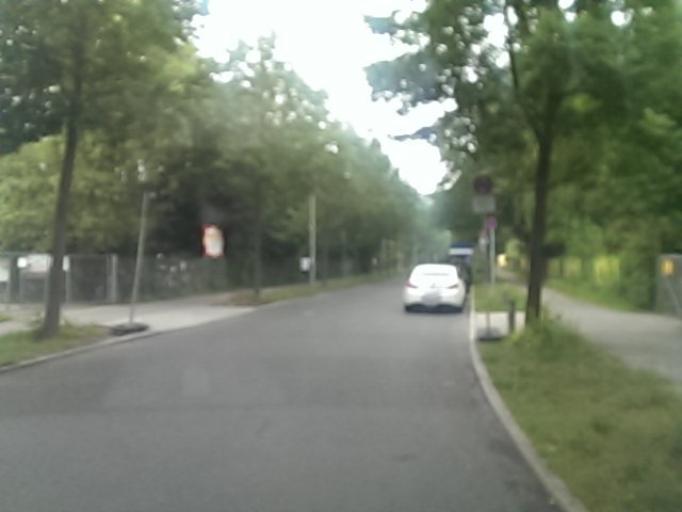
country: DE
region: Berlin
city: Zehlendorf Bezirk
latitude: 52.4320
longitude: 13.2411
